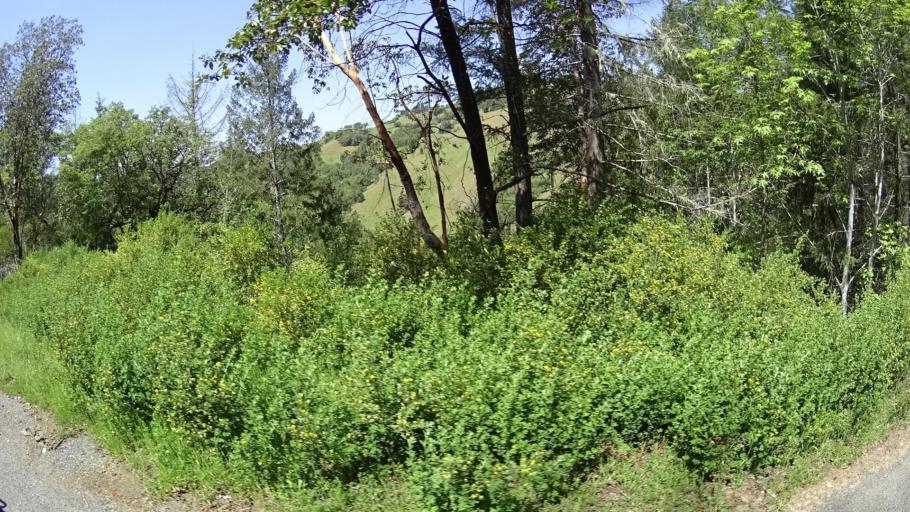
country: US
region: California
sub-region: Humboldt County
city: Redway
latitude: 40.1884
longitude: -123.5755
